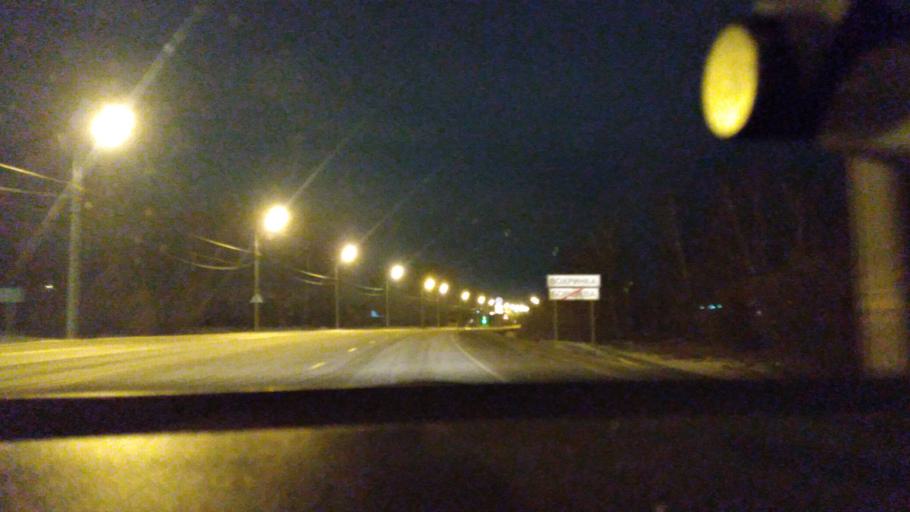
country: RU
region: Moskovskaya
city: Bronnitsy
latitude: 55.4026
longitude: 38.3049
